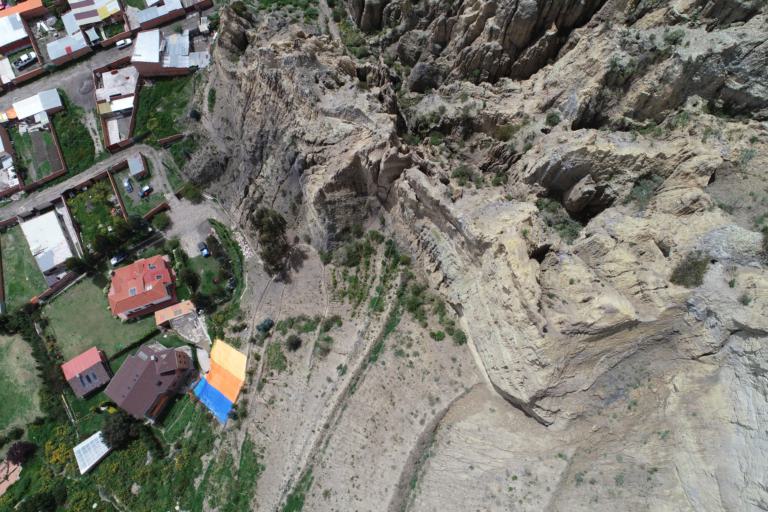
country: BO
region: La Paz
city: La Paz
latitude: -16.5008
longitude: -68.0807
